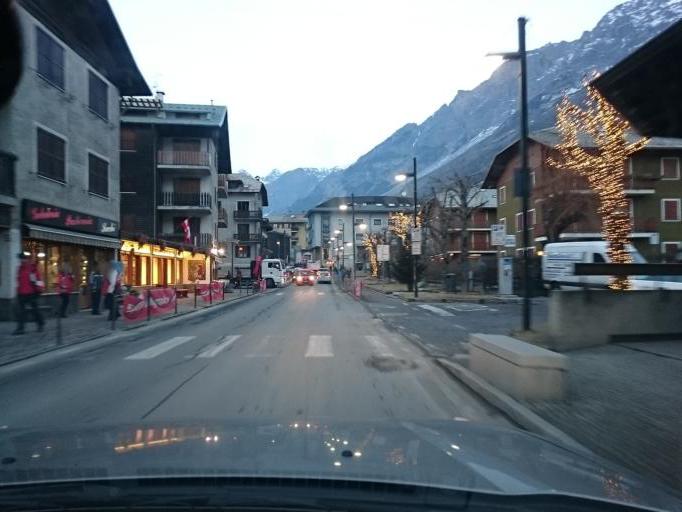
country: IT
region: Lombardy
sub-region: Provincia di Sondrio
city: Bormio
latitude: 46.4655
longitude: 10.3728
